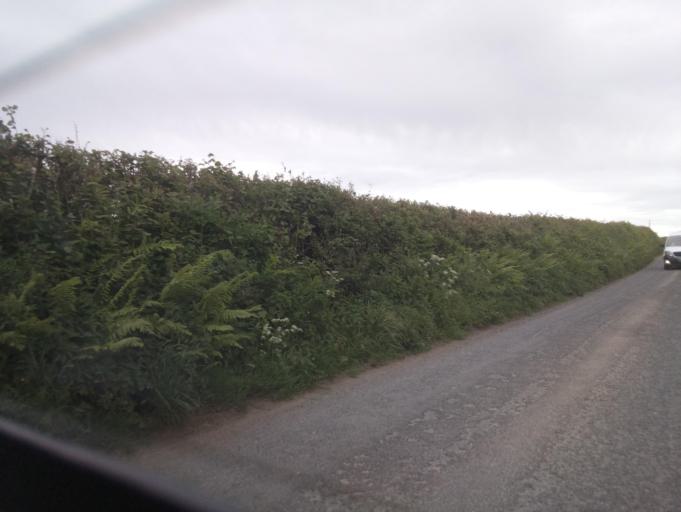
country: GB
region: England
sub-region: Devon
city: Dartmouth
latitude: 50.3222
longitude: -3.6376
